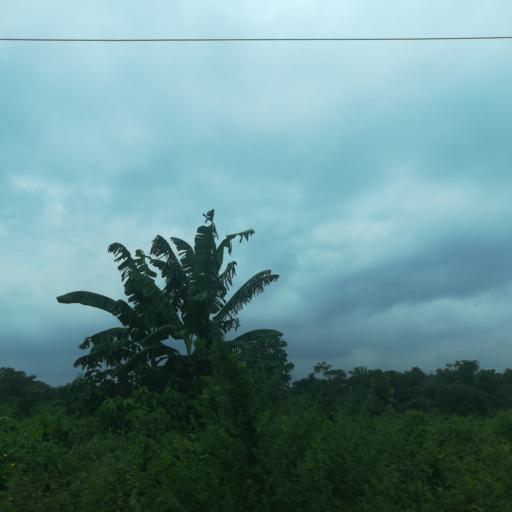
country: NG
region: Lagos
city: Ejirin
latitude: 6.6615
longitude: 3.8089
